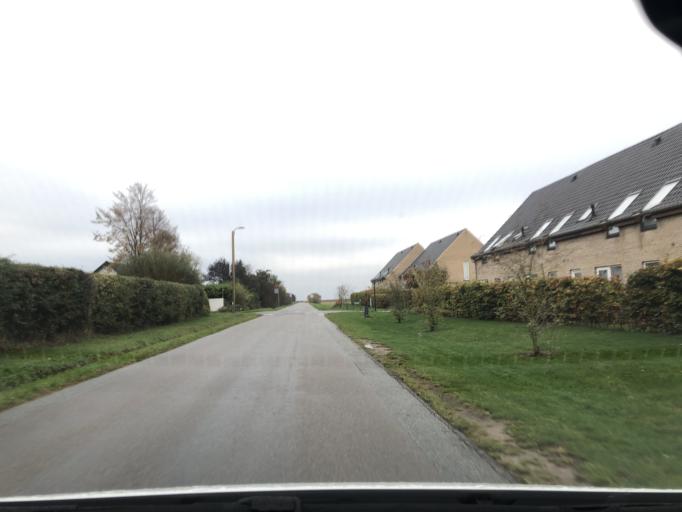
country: DK
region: Capital Region
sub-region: Dragor Kommune
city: Dragor
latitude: 55.5814
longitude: 12.6396
